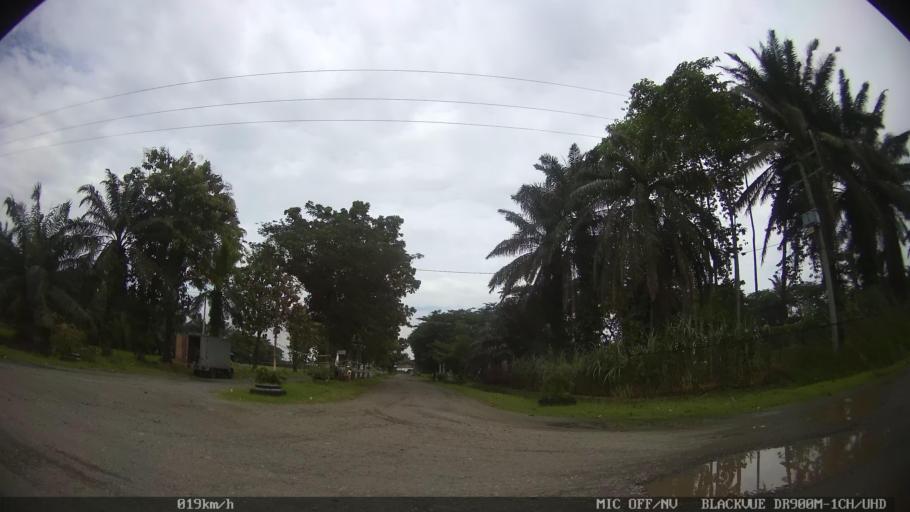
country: ID
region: North Sumatra
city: Sunggal
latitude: 3.6193
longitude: 98.5789
